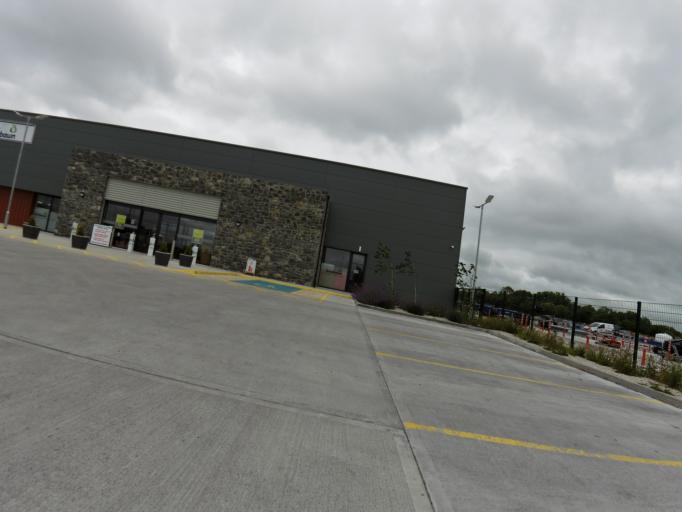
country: IE
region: Connaught
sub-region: County Galway
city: Athenry
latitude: 53.3132
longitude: -8.7355
